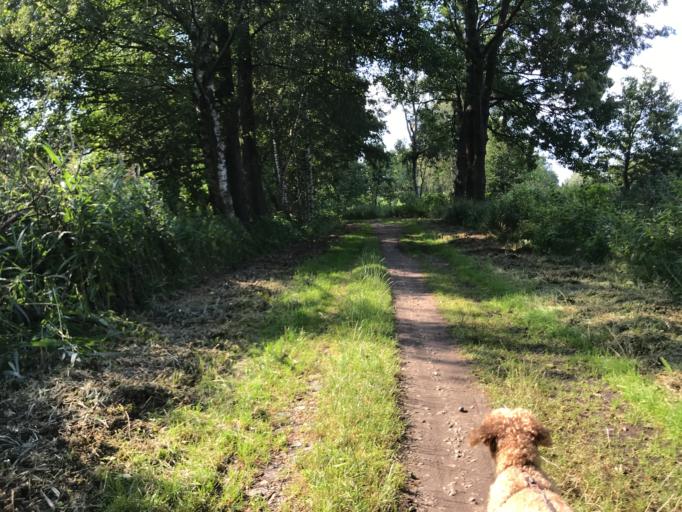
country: CZ
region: Jihocesky
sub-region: Okres Jindrichuv Hradec
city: Trebon
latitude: 49.0182
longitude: 14.7639
